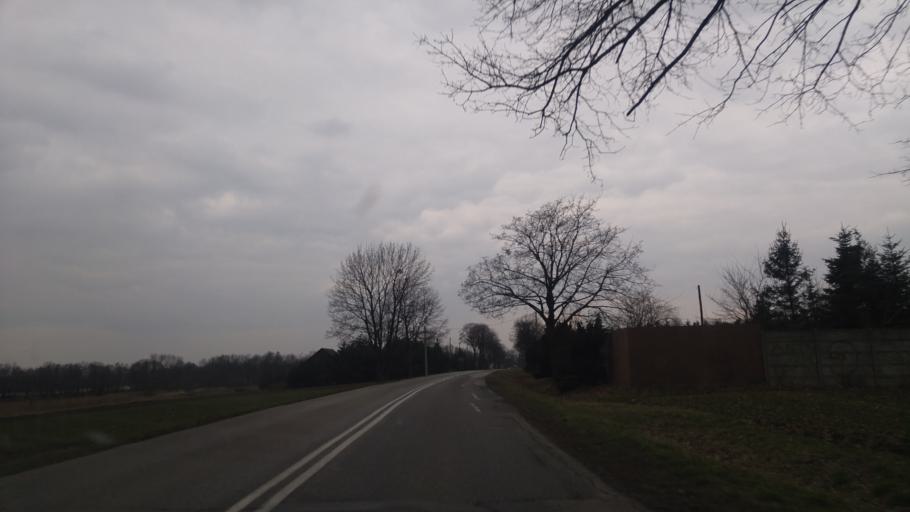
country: PL
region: Silesian Voivodeship
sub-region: Powiat cieszynski
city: Zablocie
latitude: 49.9335
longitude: 18.8044
